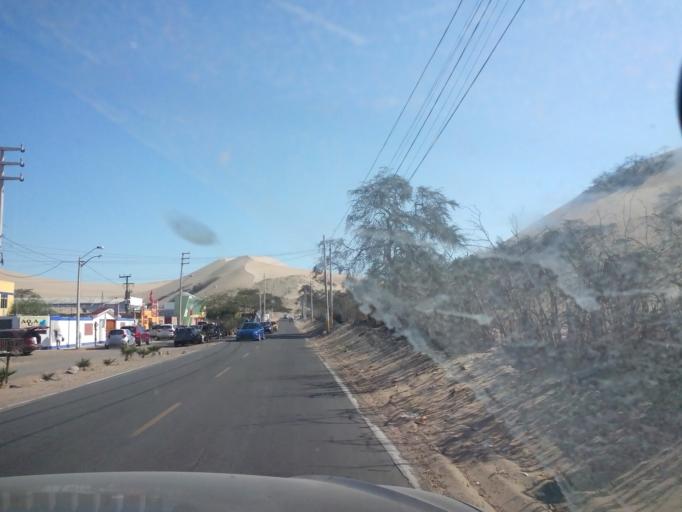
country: PE
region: Ica
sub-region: Provincia de Ica
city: Ica
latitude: -14.0853
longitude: -75.7555
